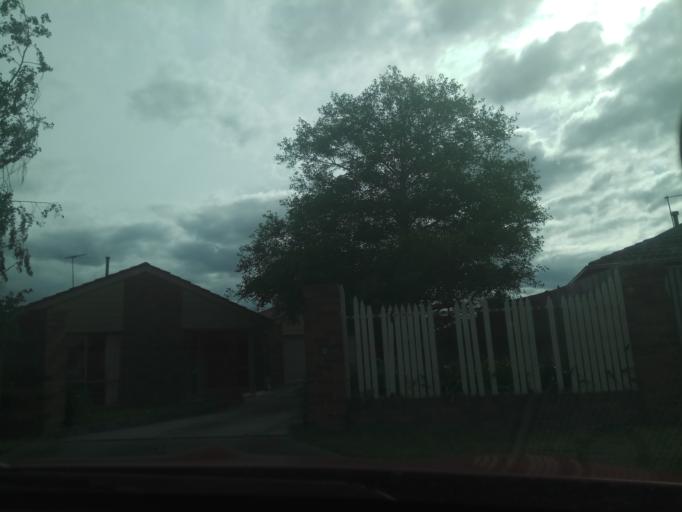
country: AU
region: Victoria
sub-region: Casey
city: Cranbourne North
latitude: -38.0703
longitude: 145.2752
